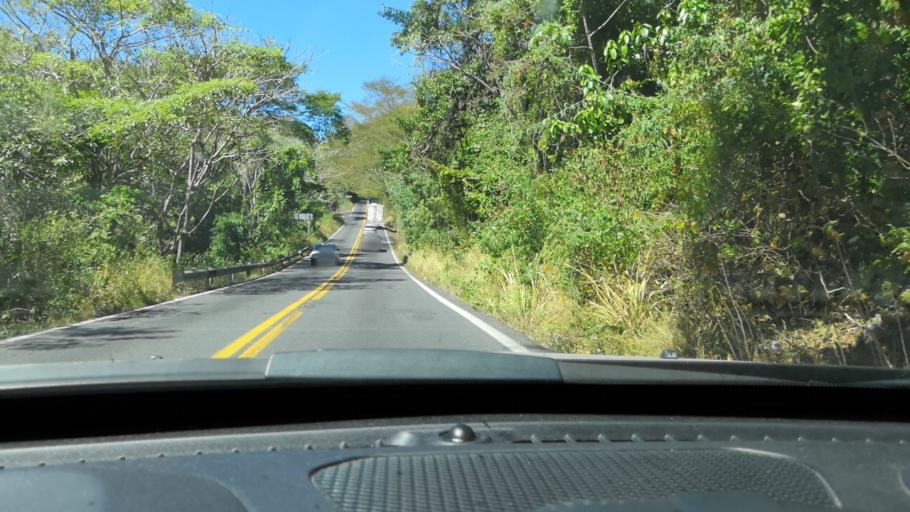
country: MX
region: Nayarit
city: Compostela
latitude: 21.2122
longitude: -104.9872
